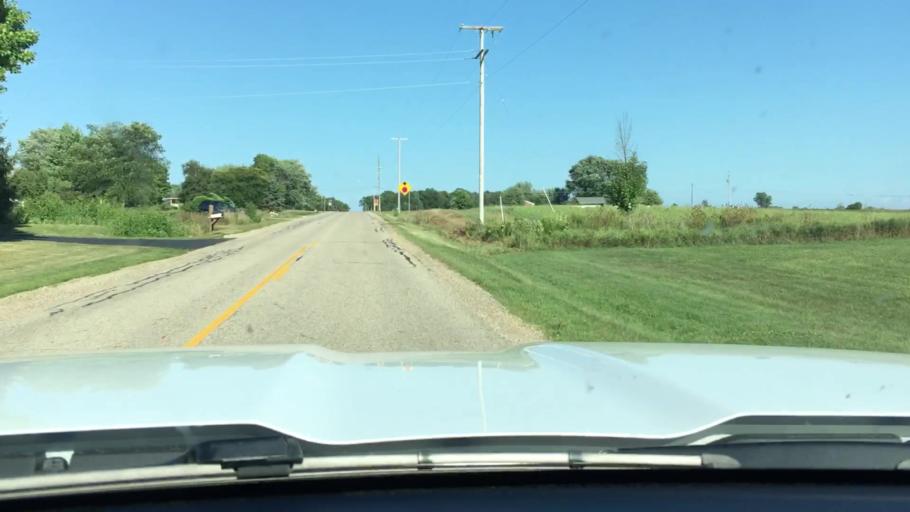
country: US
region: Michigan
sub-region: Ottawa County
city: Zeeland
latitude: 42.8264
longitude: -85.9430
